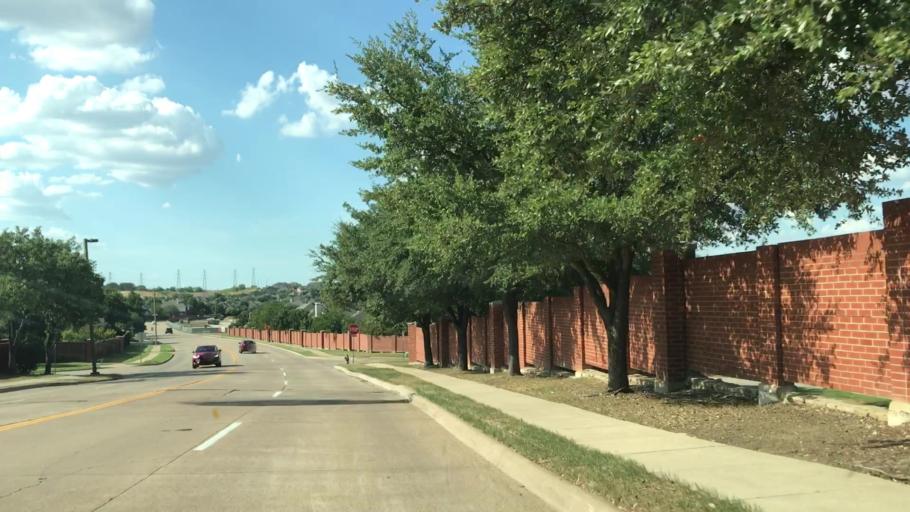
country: US
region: Texas
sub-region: Dallas County
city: Coppell
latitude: 32.9328
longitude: -96.9645
